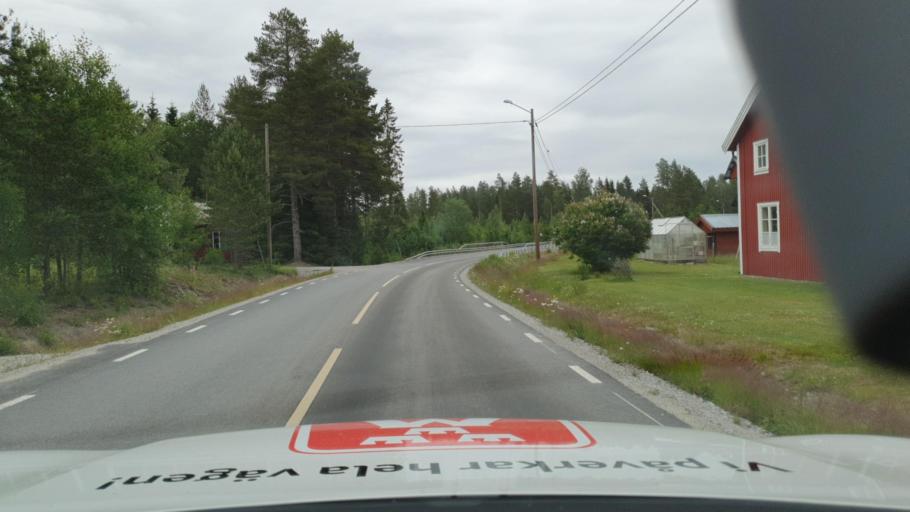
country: SE
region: Vaesterbotten
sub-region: Nordmalings Kommun
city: Nordmaling
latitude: 63.5149
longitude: 19.3471
